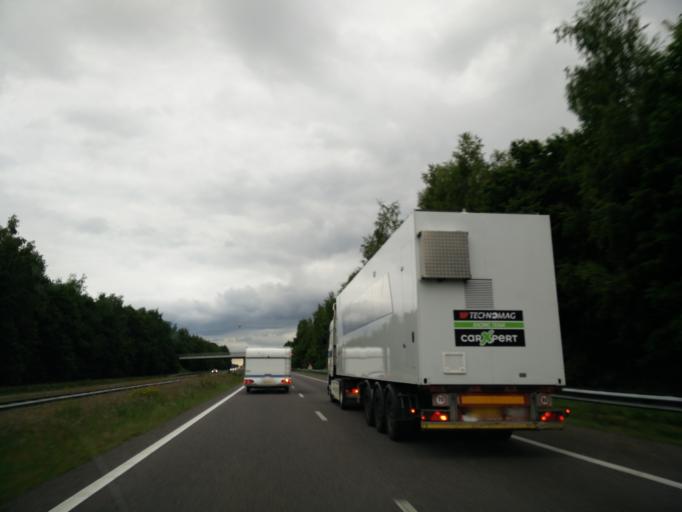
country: NL
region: Drenthe
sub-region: Gemeente Assen
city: Assen
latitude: 52.9234
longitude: 6.5338
